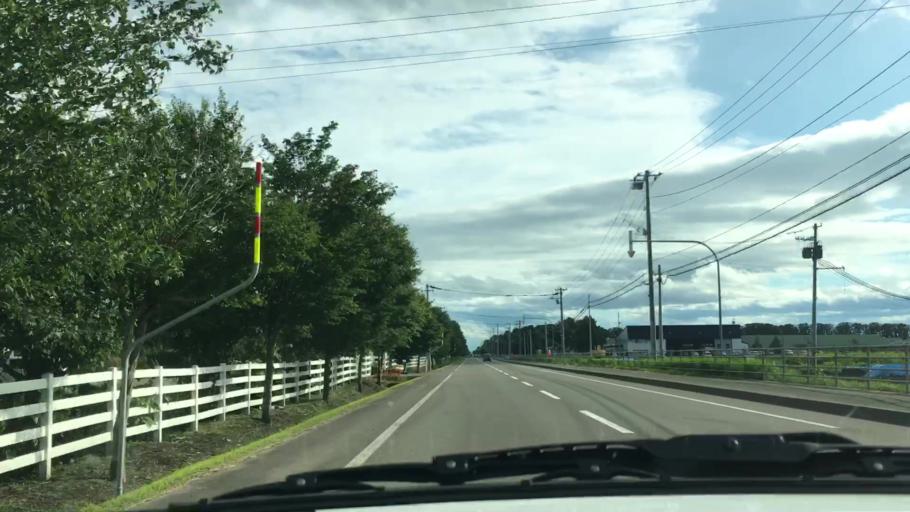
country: JP
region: Hokkaido
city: Otofuke
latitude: 43.2529
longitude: 143.2996
